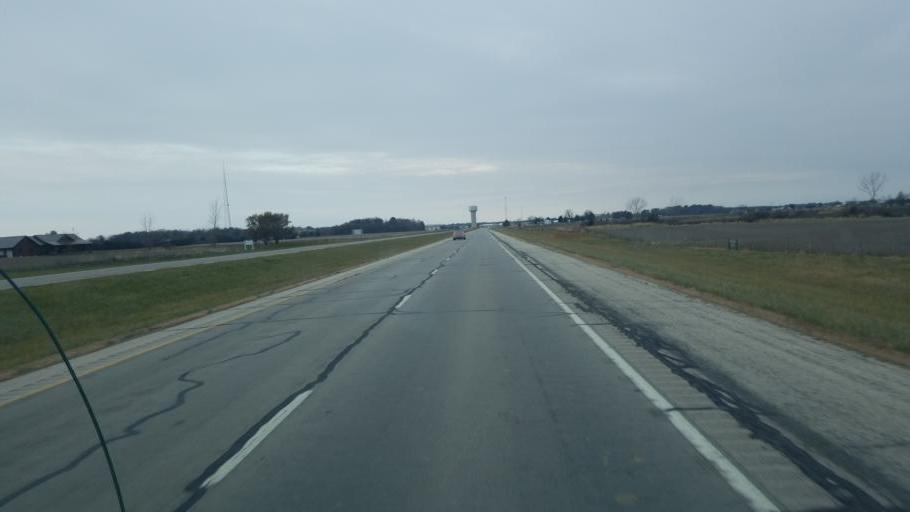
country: US
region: Ohio
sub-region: Mercer County
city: Celina
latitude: 40.5573
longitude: -84.5013
